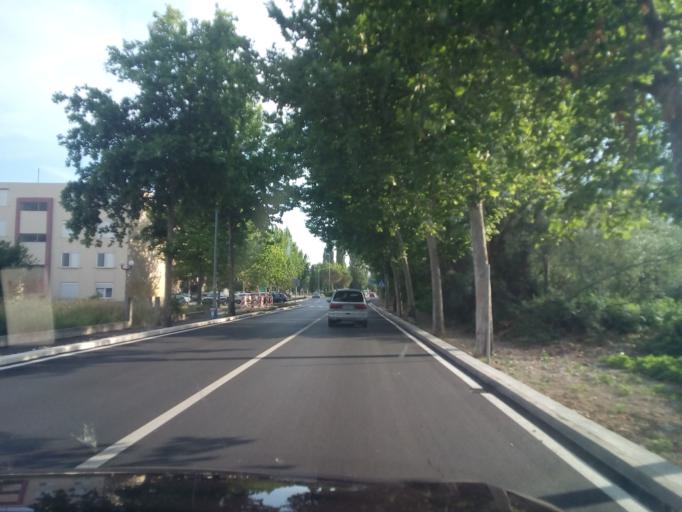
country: HR
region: Splitsko-Dalmatinska
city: Solin
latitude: 43.5371
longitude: 16.4876
